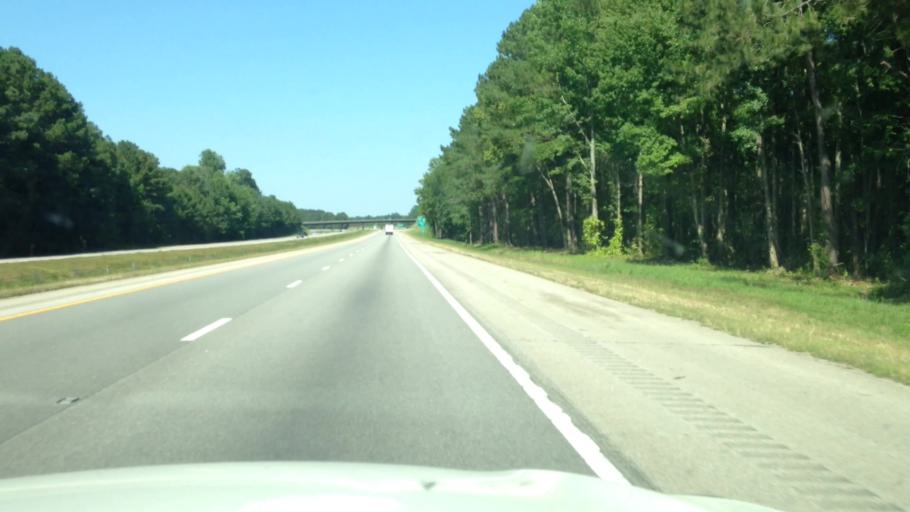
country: US
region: North Carolina
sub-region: Wilson County
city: Lucama
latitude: 35.7254
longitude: -78.0229
